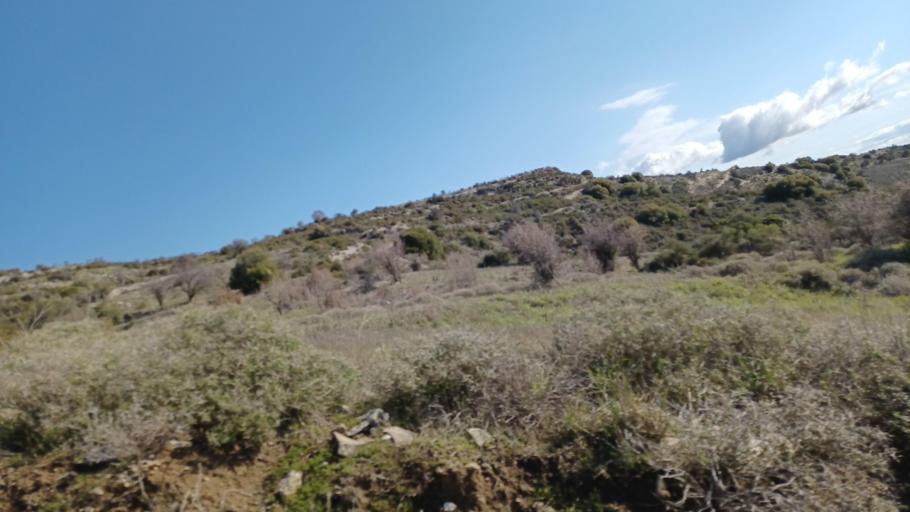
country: CY
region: Limassol
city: Pachna
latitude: 34.8204
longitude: 32.6896
